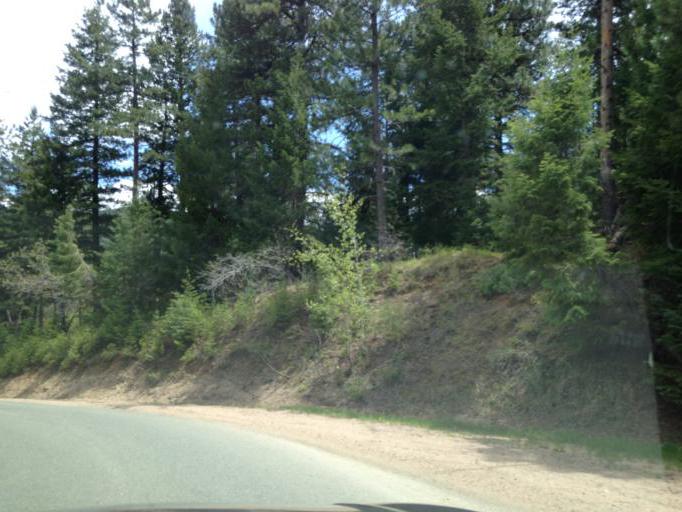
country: US
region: Colorado
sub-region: Jefferson County
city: Ken Caryl
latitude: 39.5079
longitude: -105.1885
